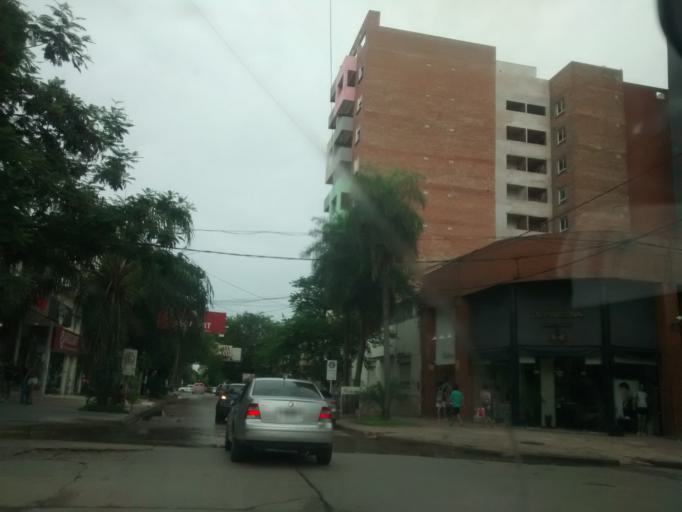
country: AR
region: Chaco
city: Resistencia
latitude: -27.4505
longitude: -58.9840
